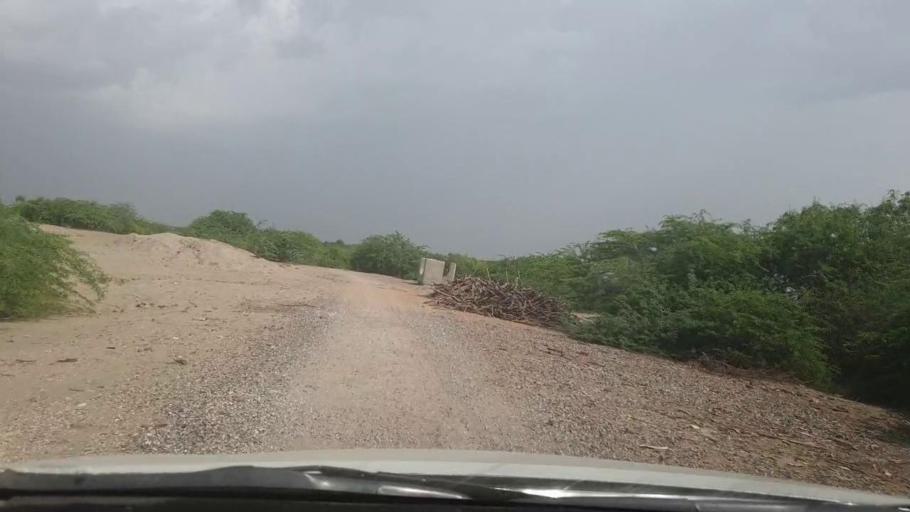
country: PK
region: Sindh
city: Kot Diji
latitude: 27.3337
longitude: 69.0487
